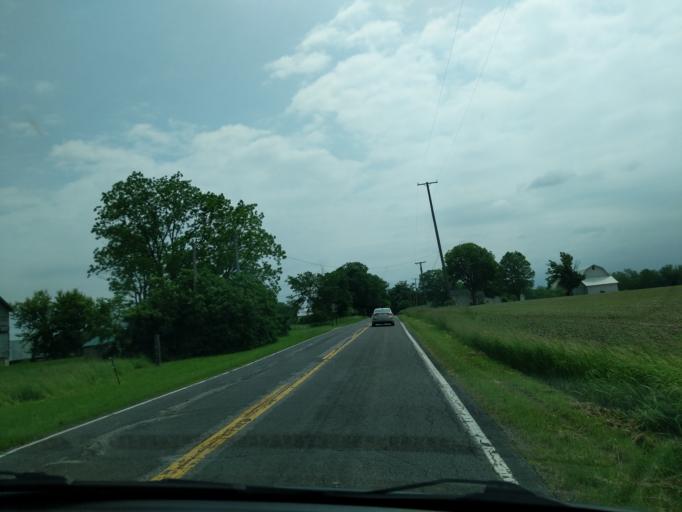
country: US
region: Michigan
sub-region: Ingham County
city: Williamston
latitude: 42.6936
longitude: -84.2481
